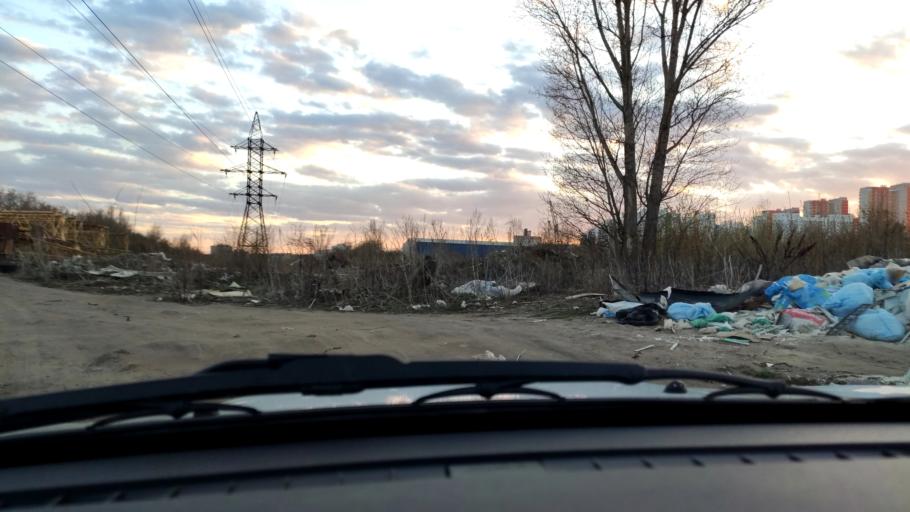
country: RU
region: Voronezj
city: Voronezh
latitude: 51.6873
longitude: 39.1451
